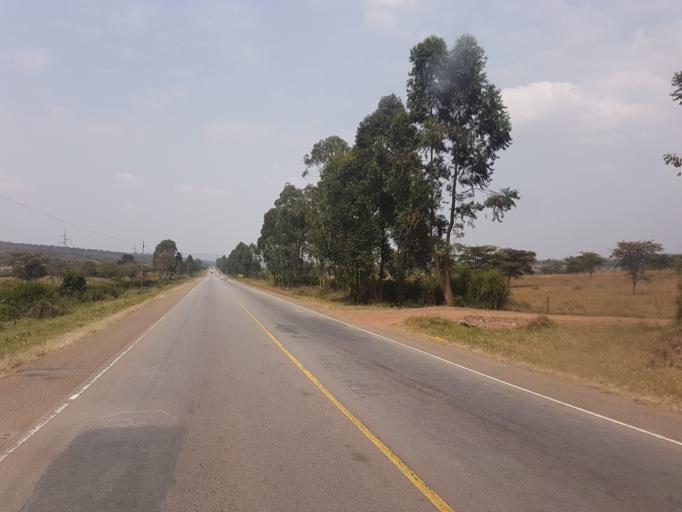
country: UG
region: Western Region
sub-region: Mbarara District
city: Mbarara
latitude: -0.5107
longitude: 30.7769
